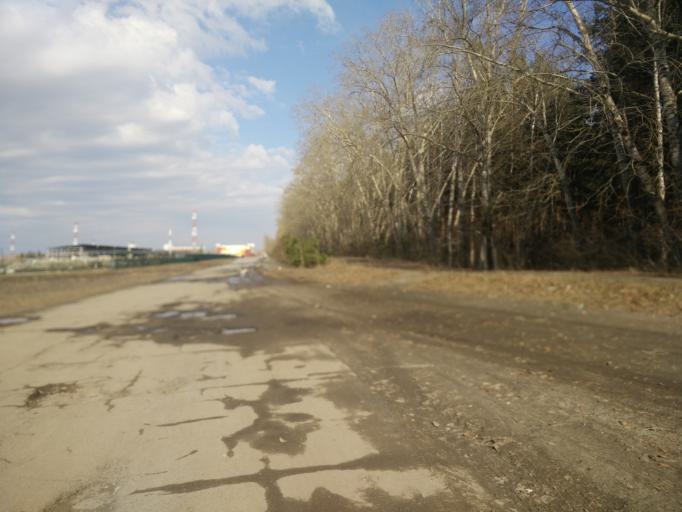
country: RU
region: Novosibirsk
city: Berdsk
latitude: 54.7609
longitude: 83.0707
